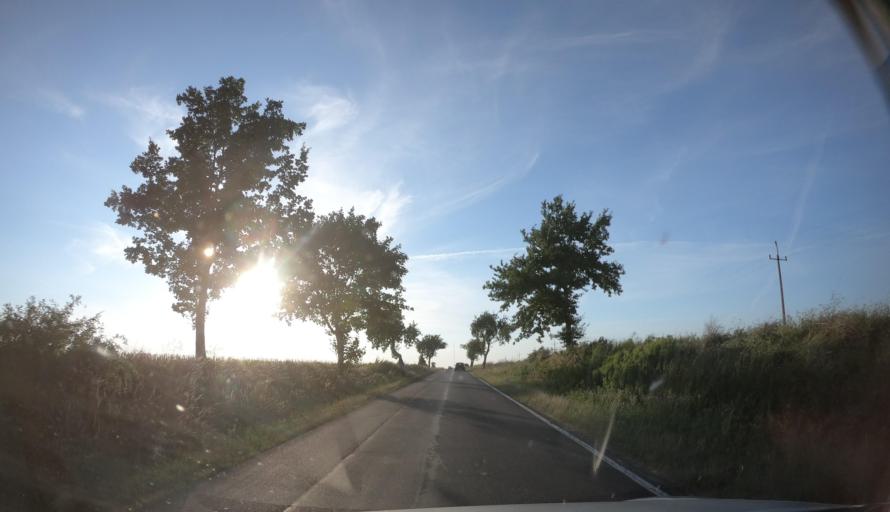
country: PL
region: Kujawsko-Pomorskie
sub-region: Powiat swiecki
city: Pruszcz
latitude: 53.2433
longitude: 18.2157
